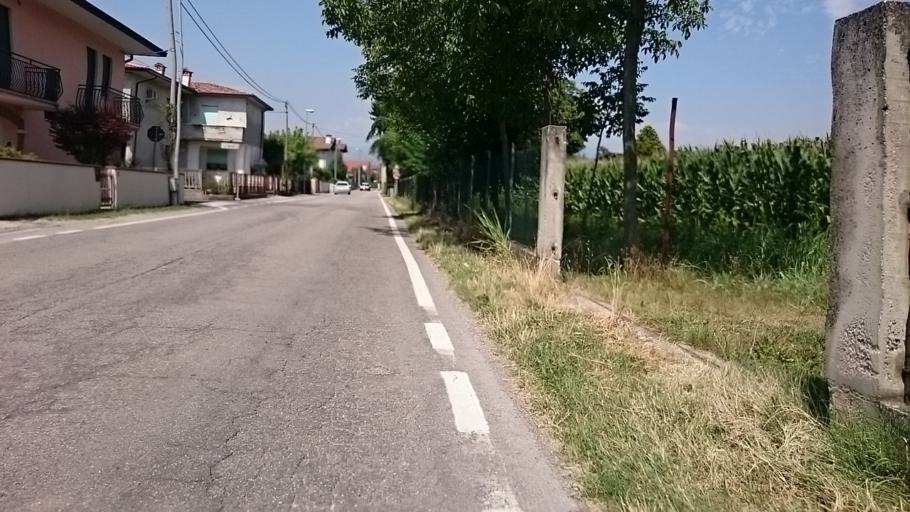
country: IT
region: Veneto
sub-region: Provincia di Vicenza
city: Rosa
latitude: 45.6845
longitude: 11.7401
